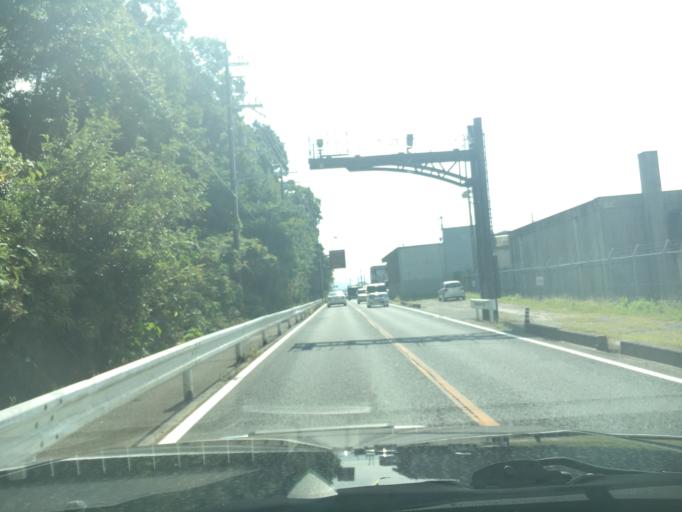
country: JP
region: Nara
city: Nara-shi
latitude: 34.7034
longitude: 135.8360
